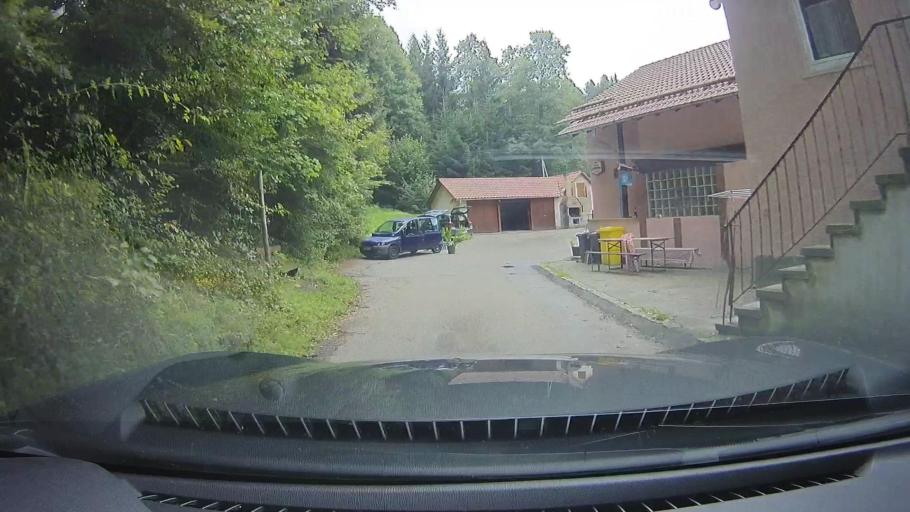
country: DE
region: Baden-Wuerttemberg
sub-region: Regierungsbezirk Stuttgart
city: Murrhardt
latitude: 48.9560
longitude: 9.5548
